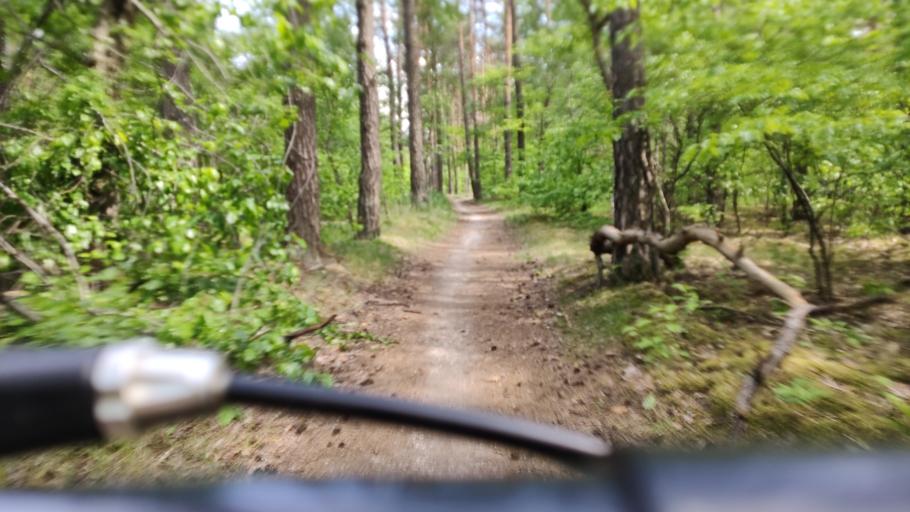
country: PL
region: Kujawsko-Pomorskie
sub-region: Wloclawek
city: Wloclawek
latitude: 52.6364
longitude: 19.1157
